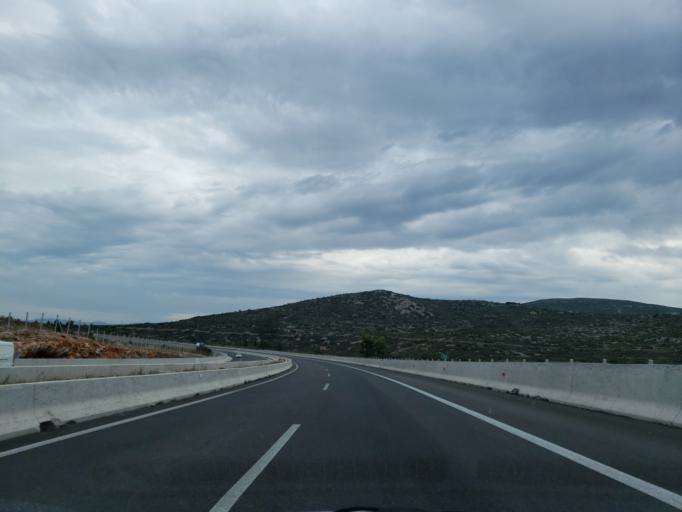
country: GR
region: Central Greece
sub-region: Nomos Voiotias
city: Akraifnia
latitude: 38.3821
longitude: 23.2467
